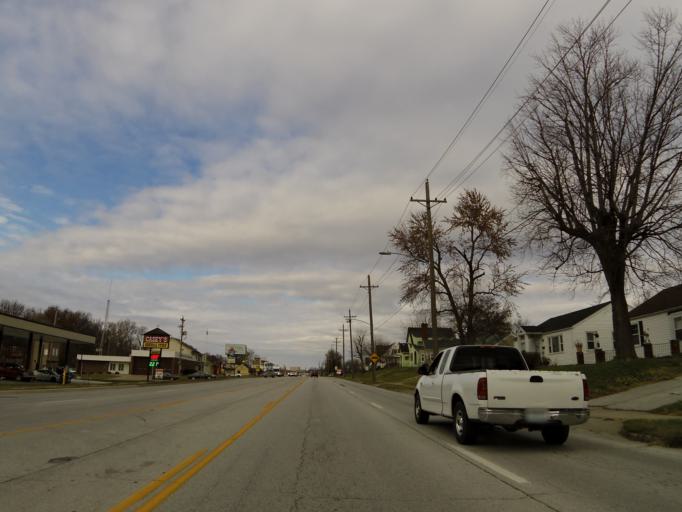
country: US
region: Missouri
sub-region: Marion County
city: Hannibal
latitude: 39.7181
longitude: -91.3920
